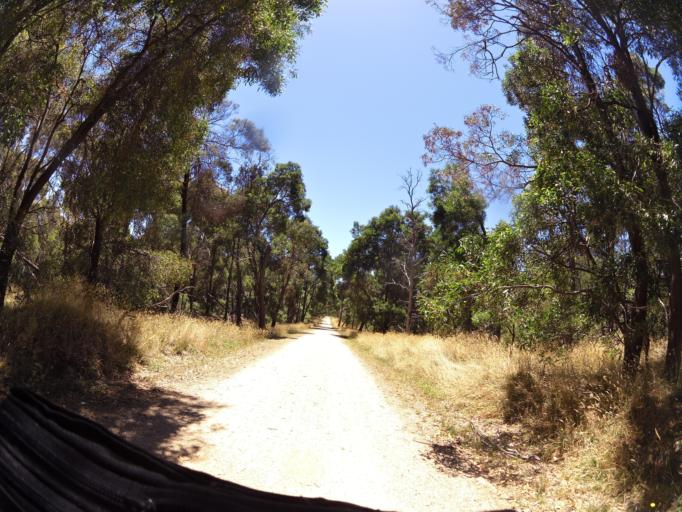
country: AU
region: Victoria
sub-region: Ballarat North
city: Delacombe
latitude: -37.6315
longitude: 143.6960
